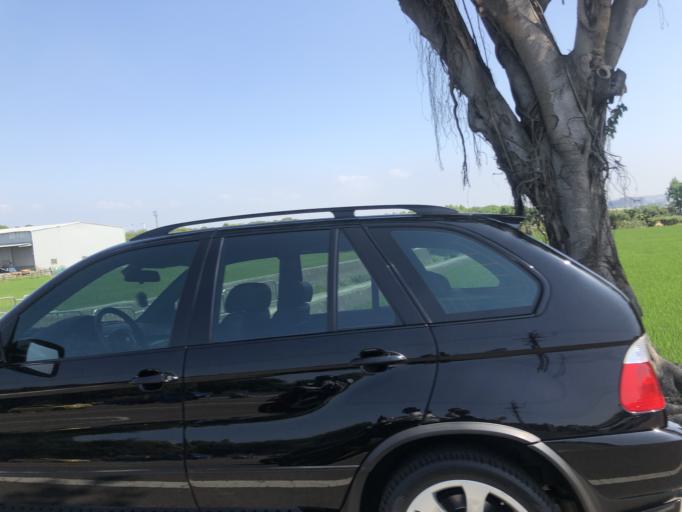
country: TW
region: Taiwan
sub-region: Taichung City
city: Taichung
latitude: 24.1393
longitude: 120.6161
